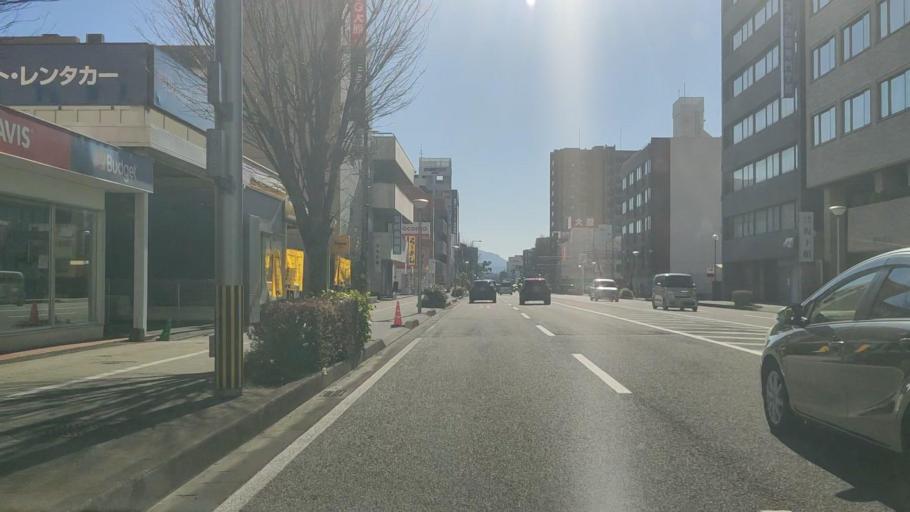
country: JP
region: Miyazaki
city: Miyazaki-shi
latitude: 31.9144
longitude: 131.4303
